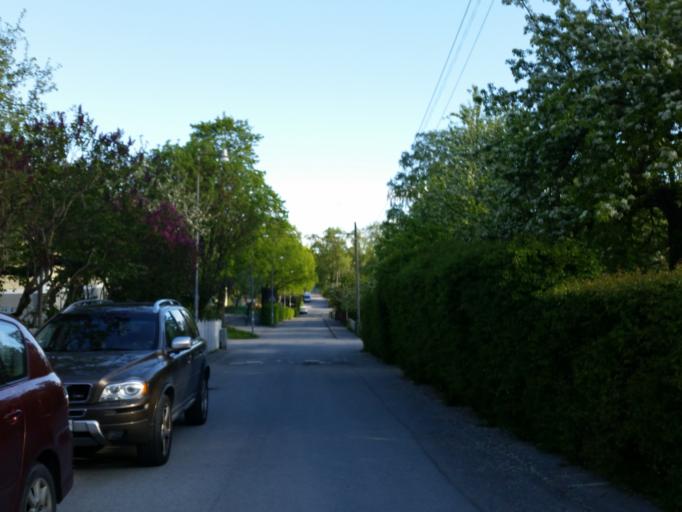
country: SE
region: Stockholm
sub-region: Sundbybergs Kommun
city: Sundbyberg
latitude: 59.3728
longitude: 17.9544
